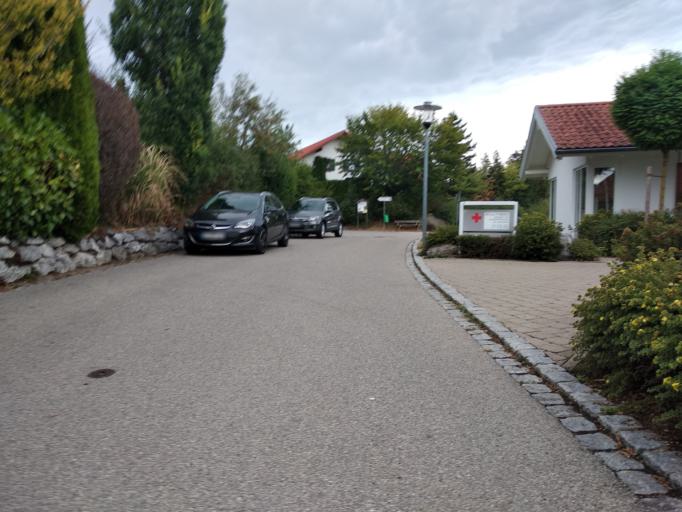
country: DE
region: Bavaria
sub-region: Swabia
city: Haldenwang
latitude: 47.8197
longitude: 10.3341
